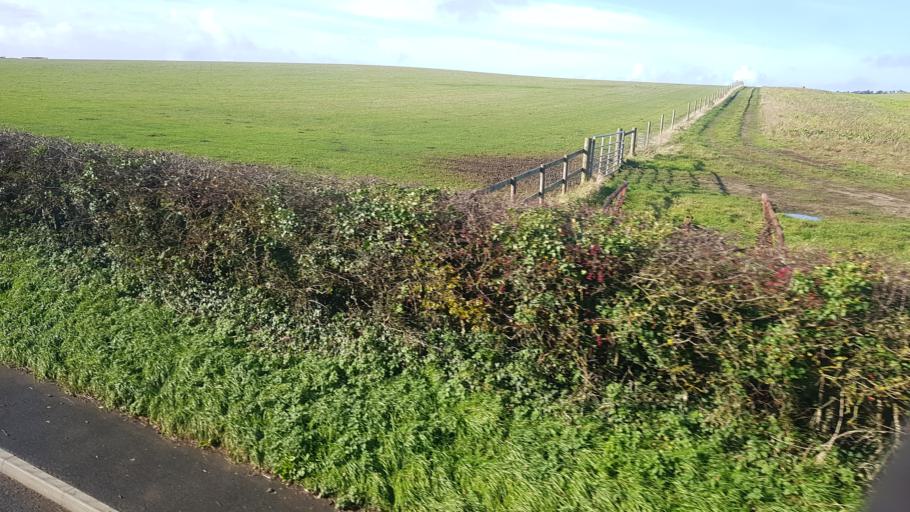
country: GB
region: England
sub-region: Isle of Wight
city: Chale
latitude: 50.6431
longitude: -1.3634
